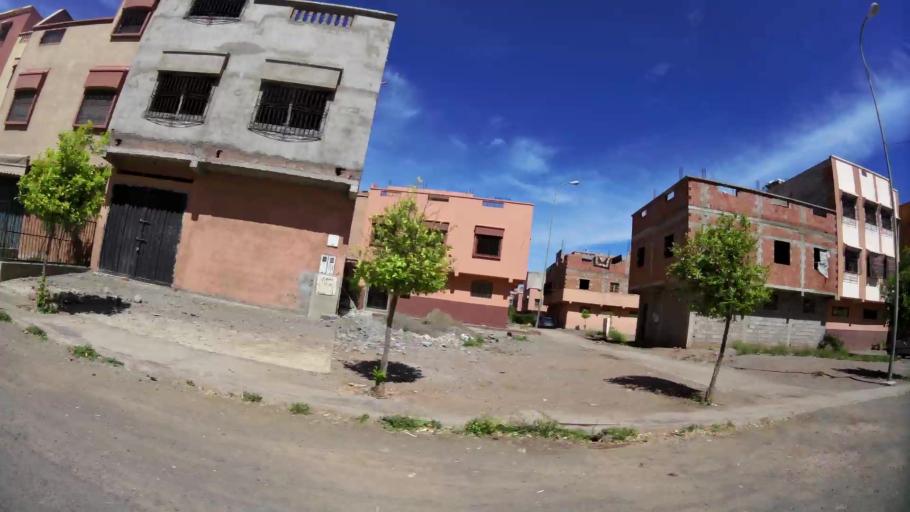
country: MA
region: Marrakech-Tensift-Al Haouz
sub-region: Marrakech
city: Marrakesh
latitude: 31.6381
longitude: -8.1093
